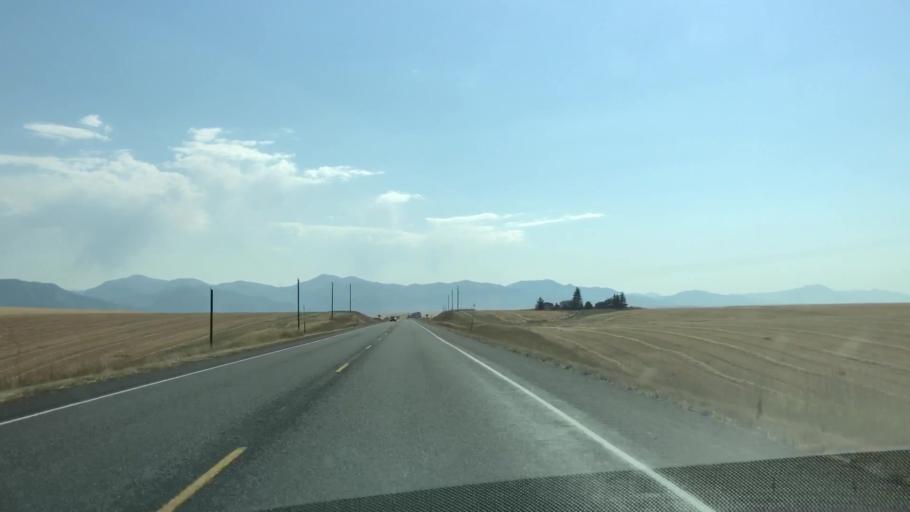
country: US
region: Idaho
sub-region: Madison County
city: Rexburg
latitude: 43.5862
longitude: -111.5958
